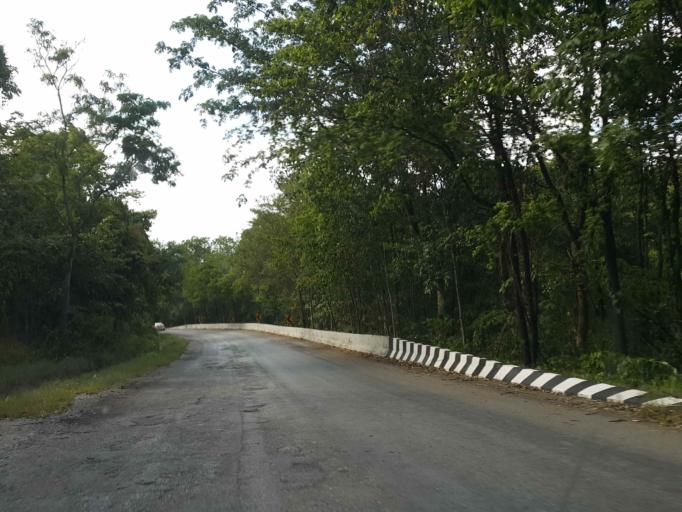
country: TH
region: Lampang
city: Thoen
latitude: 17.6255
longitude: 99.3130
